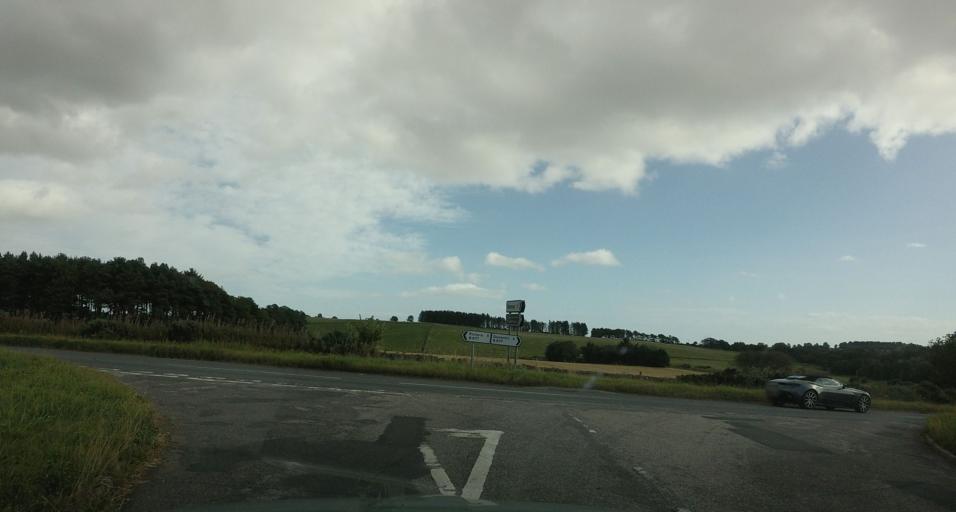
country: GB
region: Scotland
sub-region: Aberdeenshire
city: Kemnay
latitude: 57.1757
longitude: -2.4100
